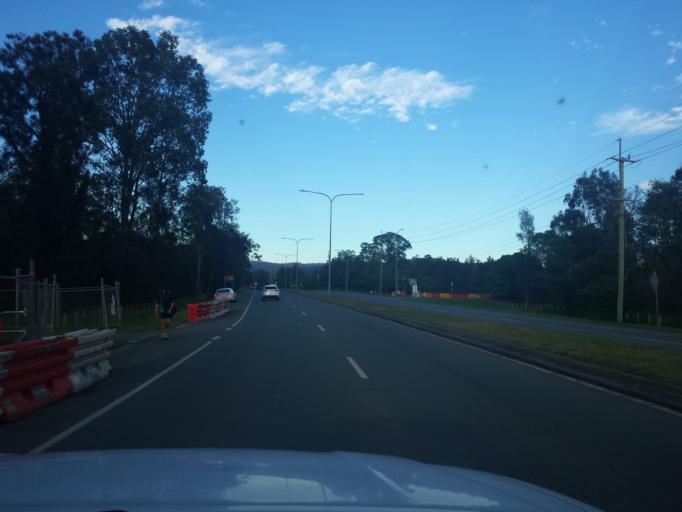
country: AU
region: Queensland
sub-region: Gold Coast
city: Oxenford
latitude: -27.8810
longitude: 153.3310
